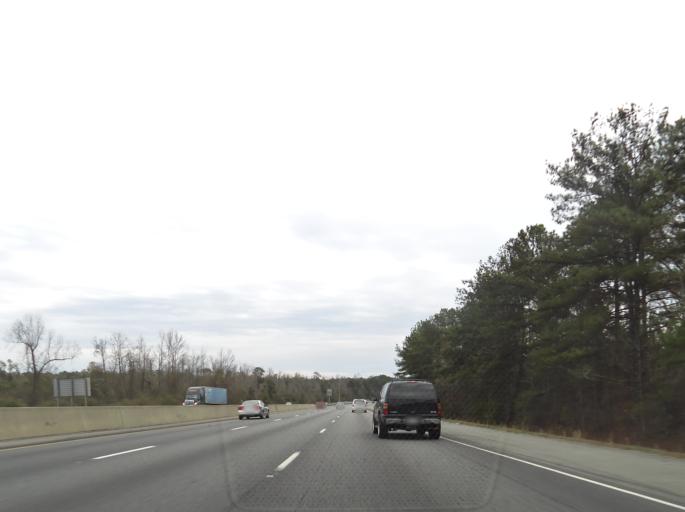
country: US
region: Georgia
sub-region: Bibb County
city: West Point
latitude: 32.8040
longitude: -83.7231
